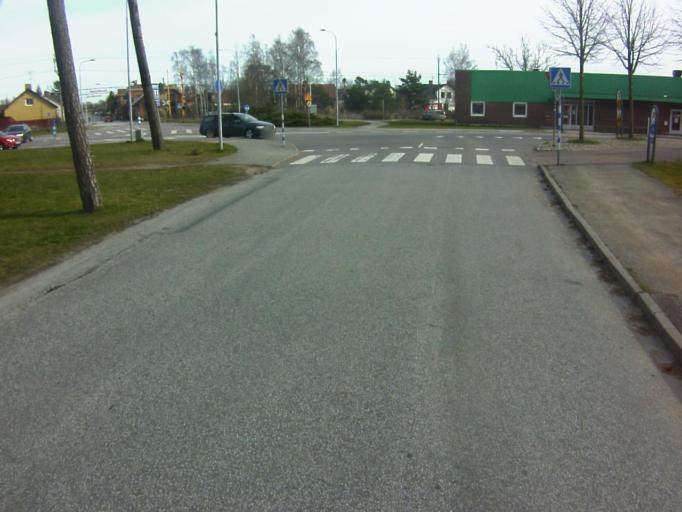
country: SE
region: Skane
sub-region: Kavlinge Kommun
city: Kaevlinge
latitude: 55.7766
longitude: 13.0978
